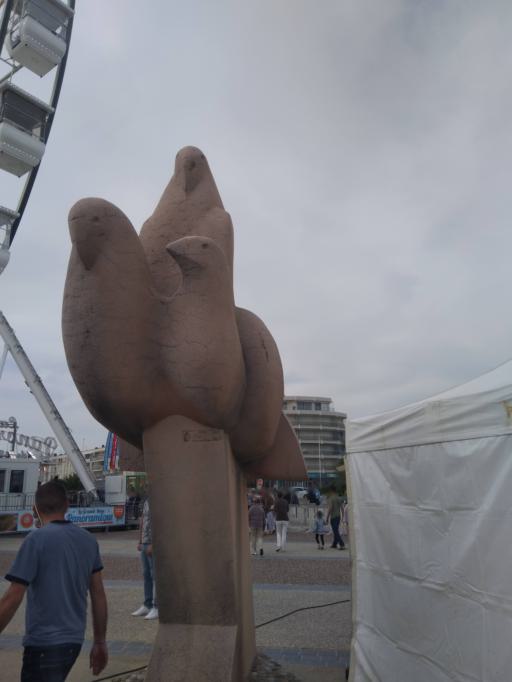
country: FR
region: Pays de la Loire
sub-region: Departement de la Vendee
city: Saint-Jean-de-Monts
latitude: 46.7810
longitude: -2.0679
